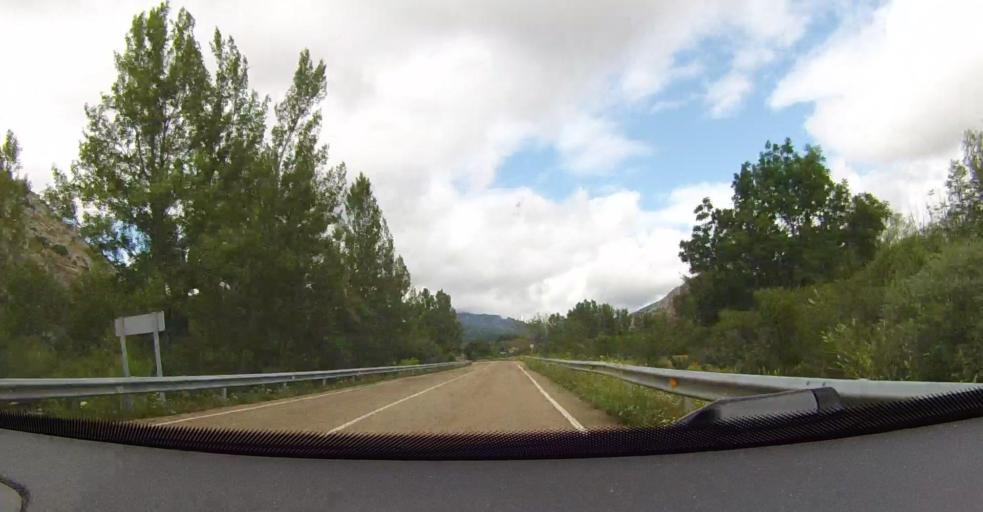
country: ES
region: Castille and Leon
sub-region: Provincia de Leon
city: Puebla de Lillo
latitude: 42.9947
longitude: -5.2631
